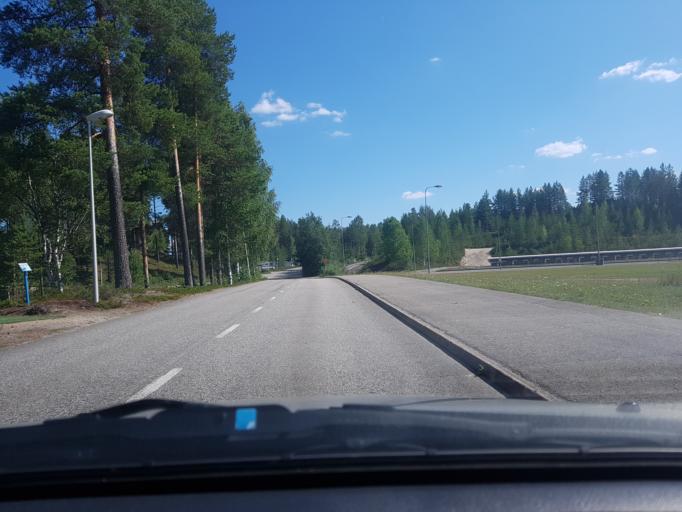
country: FI
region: Kainuu
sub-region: Kehys-Kainuu
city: Kuhmo
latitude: 64.1193
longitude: 29.5841
